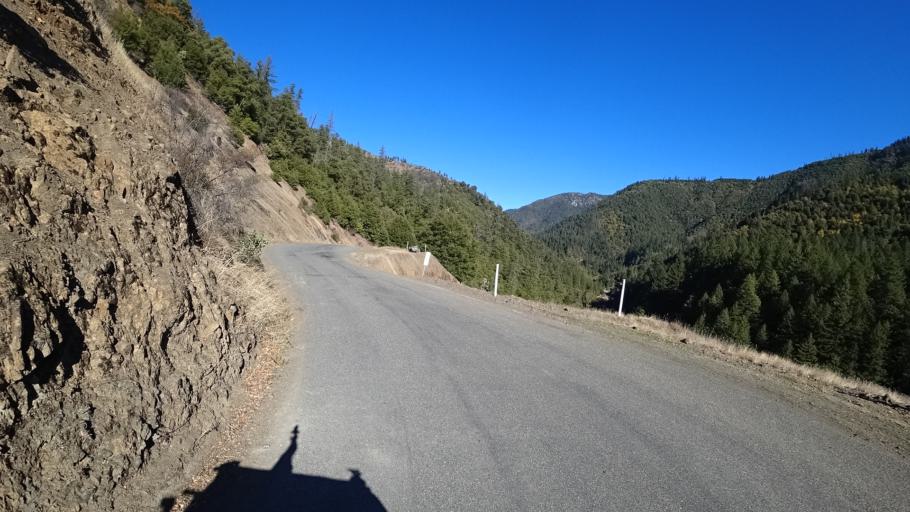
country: US
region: California
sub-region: Humboldt County
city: Willow Creek
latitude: 41.2730
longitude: -123.2941
